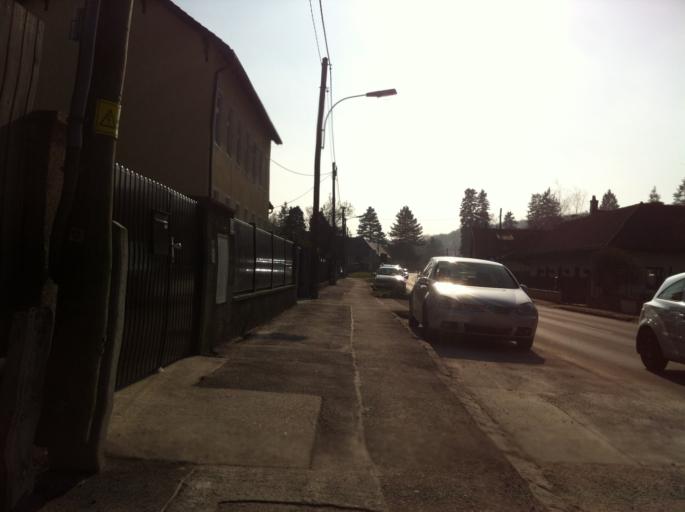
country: AT
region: Lower Austria
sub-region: Politischer Bezirk Wien-Umgebung
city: Wolfsgraben
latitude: 48.1924
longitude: 16.1329
